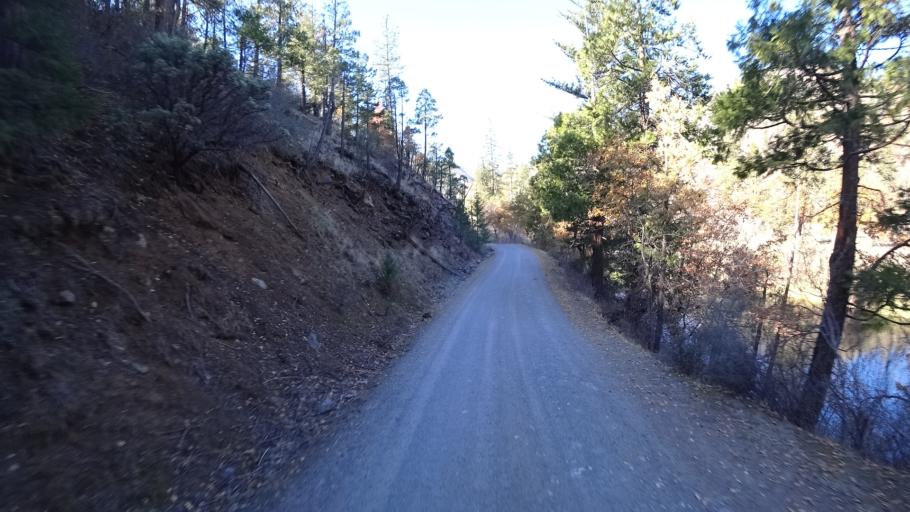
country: US
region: California
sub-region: Siskiyou County
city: Yreka
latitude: 41.8363
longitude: -122.8374
